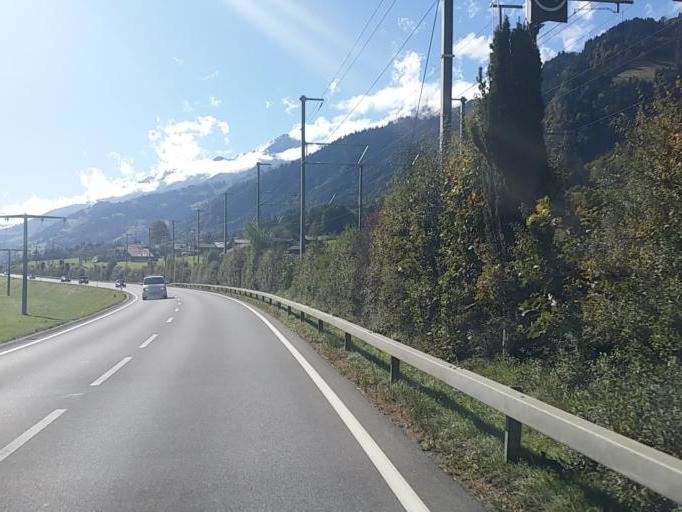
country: CH
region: Bern
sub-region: Frutigen-Niedersimmental District
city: Frutigen
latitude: 46.6162
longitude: 7.6789
